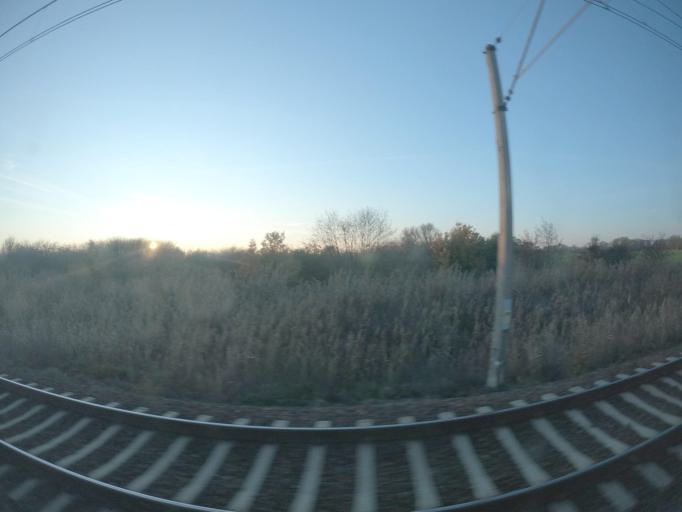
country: PL
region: Lubusz
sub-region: Powiat slubicki
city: Gorzyca
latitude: 52.5341
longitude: 14.6507
